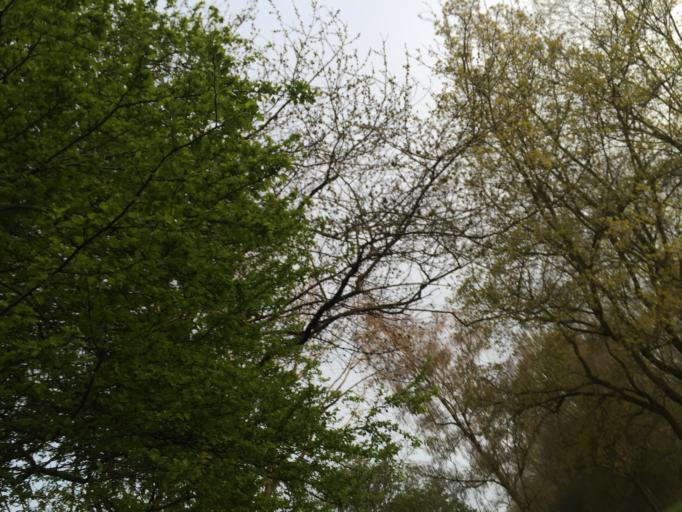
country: DK
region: South Denmark
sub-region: Odense Kommune
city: Odense
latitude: 55.3768
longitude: 10.4067
